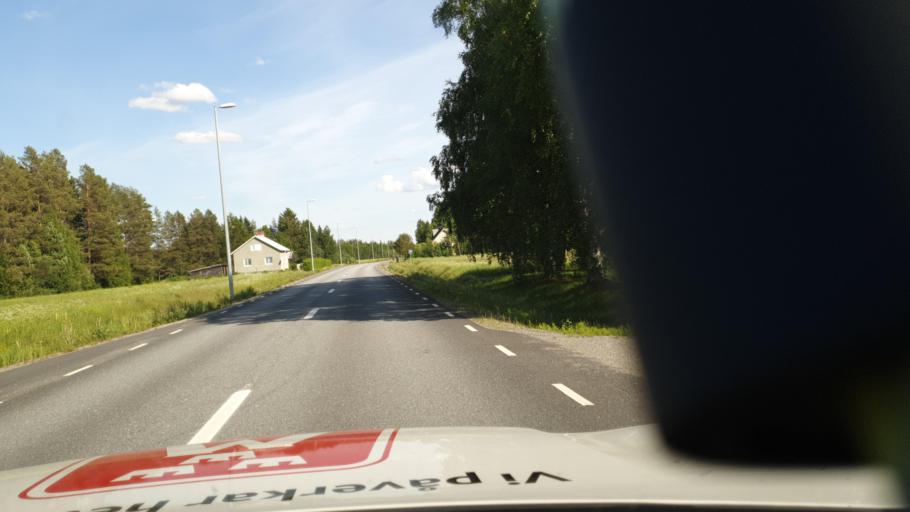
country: SE
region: Vaesterbotten
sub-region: Skelleftea Kommun
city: Forsbacka
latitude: 64.6995
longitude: 20.4696
